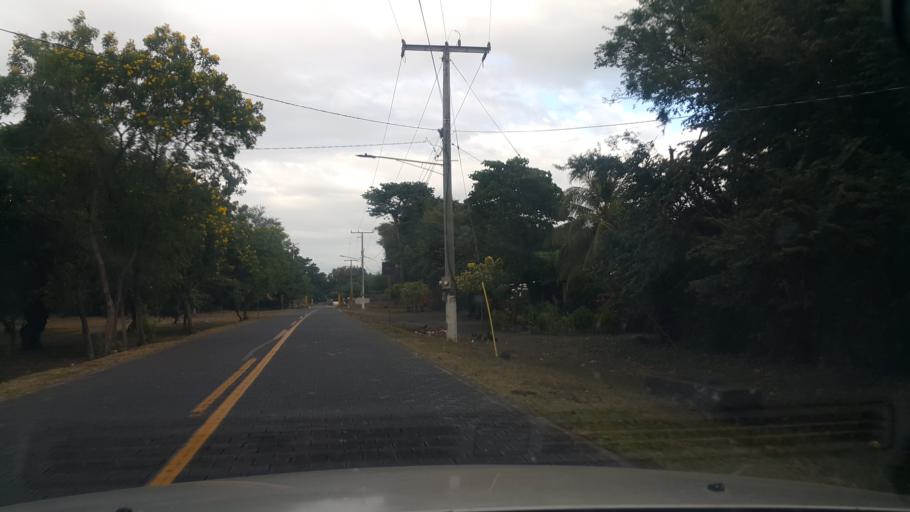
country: NI
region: Rivas
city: Moyogalpa
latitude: 11.5216
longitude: -85.7039
